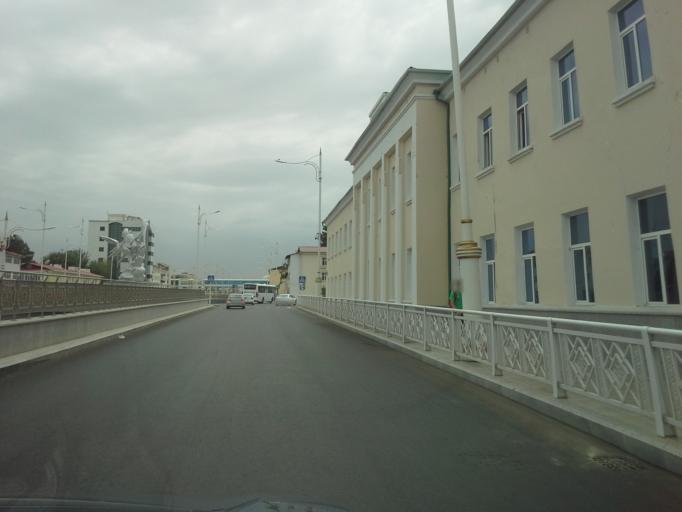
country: TM
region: Ahal
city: Ashgabat
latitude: 37.9377
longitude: 58.3985
